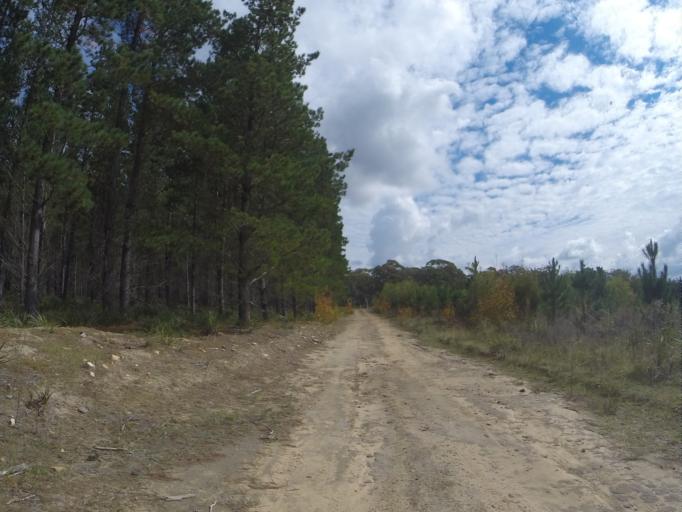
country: AU
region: New South Wales
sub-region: Wingecarribee
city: Moss Vale
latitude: -34.5269
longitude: 150.2258
